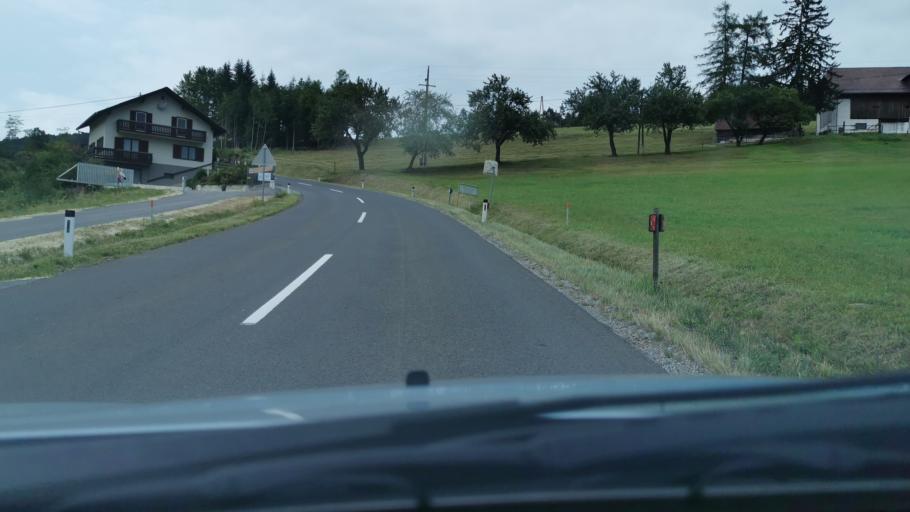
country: AT
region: Styria
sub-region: Politischer Bezirk Weiz
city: Fischbach
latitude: 47.3951
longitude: 15.6682
